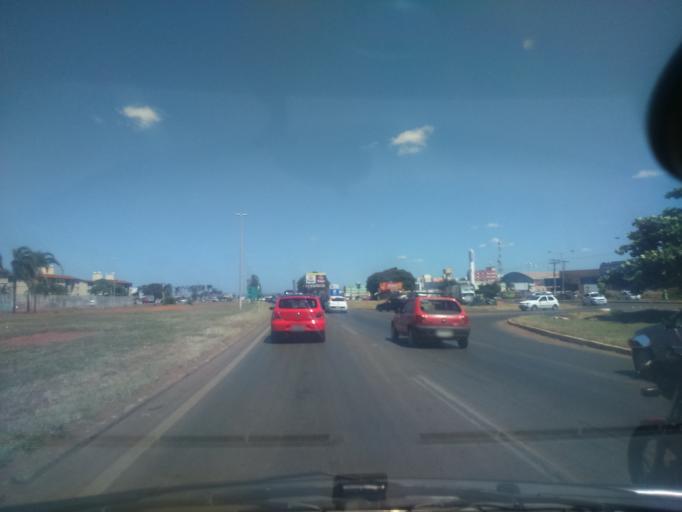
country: BR
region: Goias
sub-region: Luziania
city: Luziania
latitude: -16.0712
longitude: -47.9852
